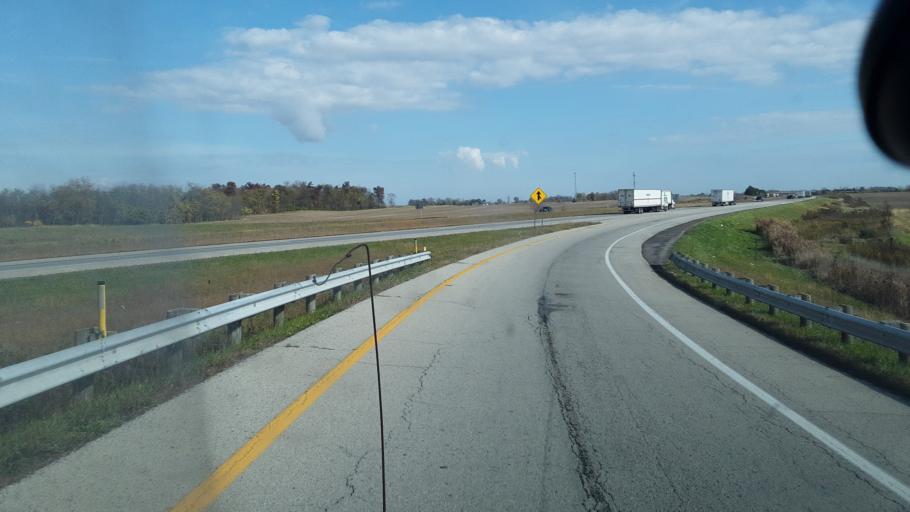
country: US
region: Ohio
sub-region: Greene County
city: Jamestown
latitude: 39.5575
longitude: -83.7177
